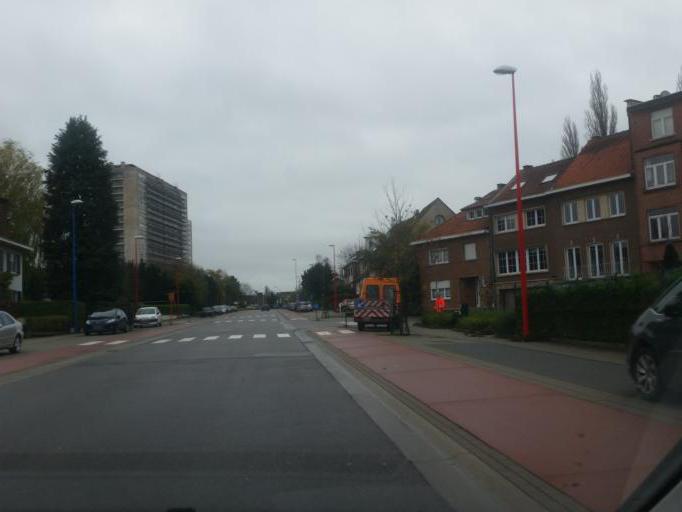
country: BE
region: Flanders
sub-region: Provincie Vlaams-Brabant
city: Grimbergen
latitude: 50.9037
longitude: 4.3571
